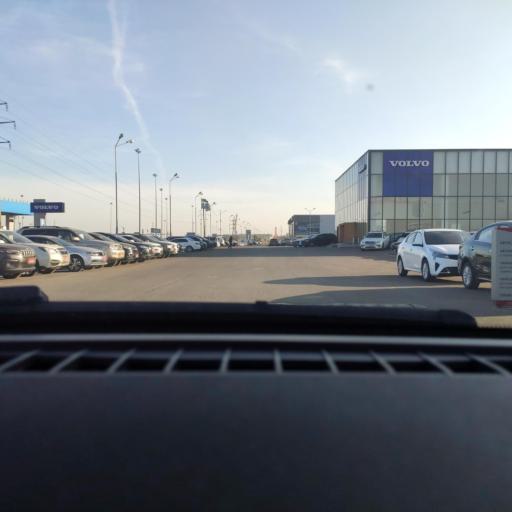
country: RU
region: Voronezj
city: Somovo
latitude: 51.6637
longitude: 39.3003
